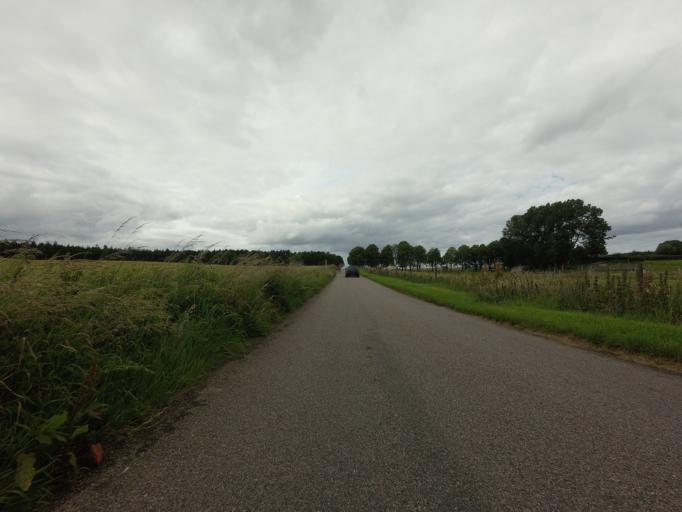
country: GB
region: Scotland
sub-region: Moray
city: Forres
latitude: 57.6002
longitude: -3.7215
